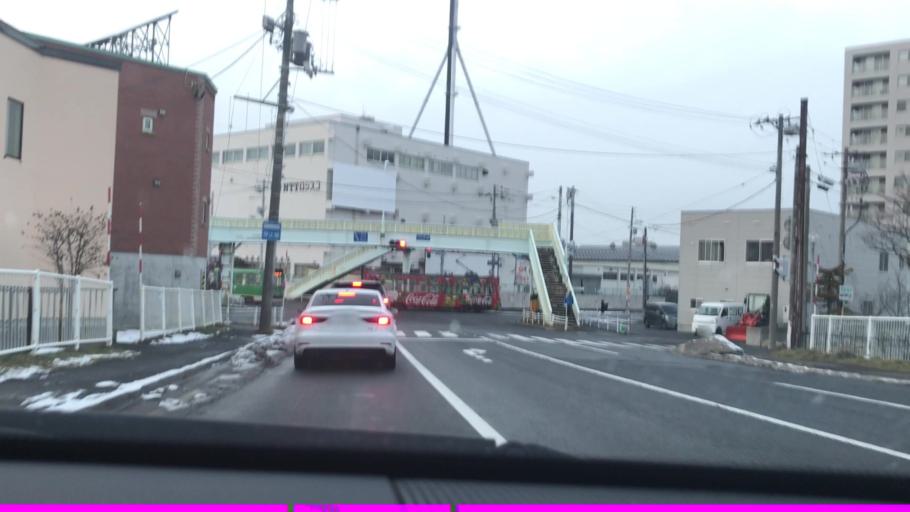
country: JP
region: Hokkaido
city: Sapporo
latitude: 43.0309
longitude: 141.3527
